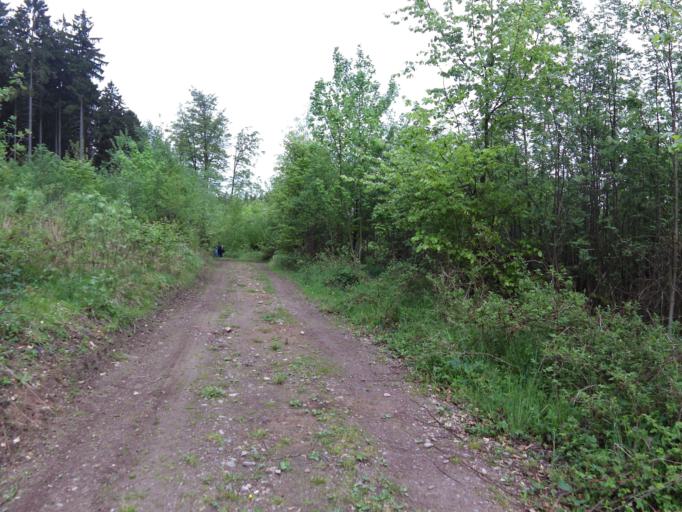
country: DE
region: Thuringia
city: Herrenhof
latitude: 50.8199
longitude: 10.6758
